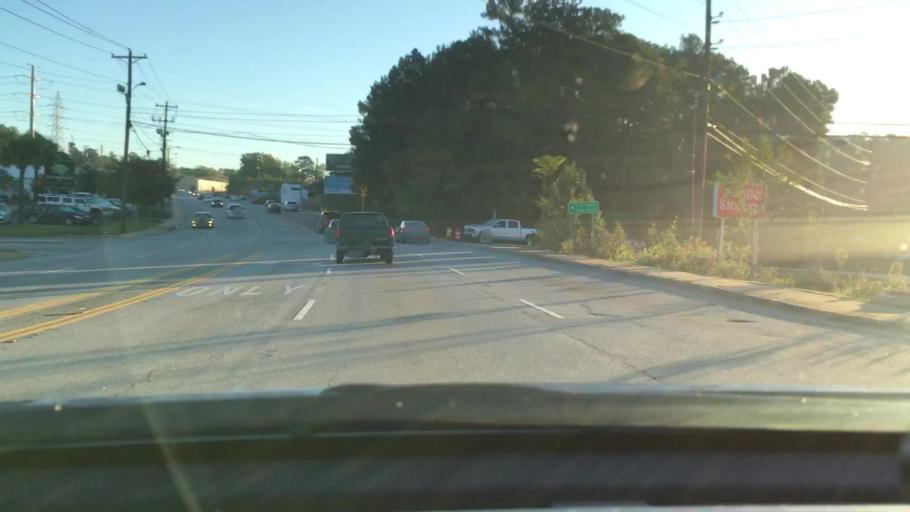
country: US
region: South Carolina
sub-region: Lexington County
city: West Columbia
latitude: 34.0272
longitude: -81.0628
